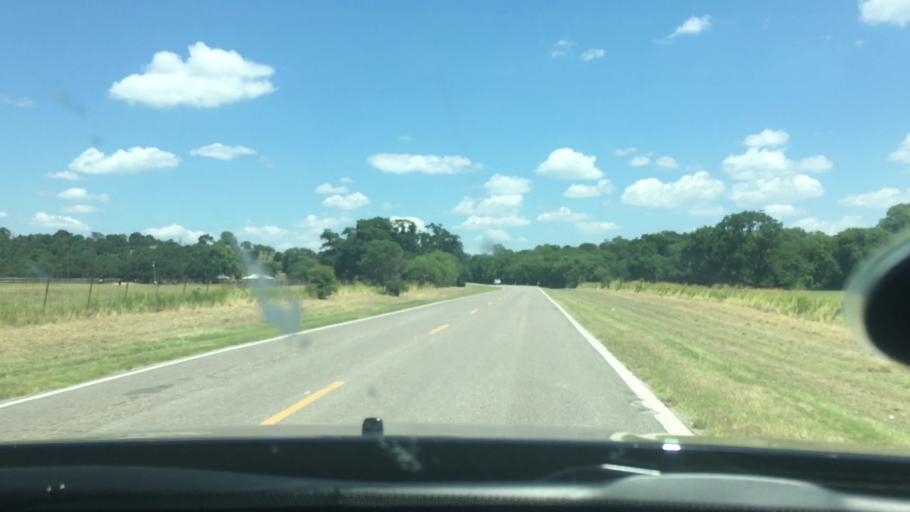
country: US
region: Oklahoma
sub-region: Carter County
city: Dickson
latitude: 34.3040
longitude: -96.9640
